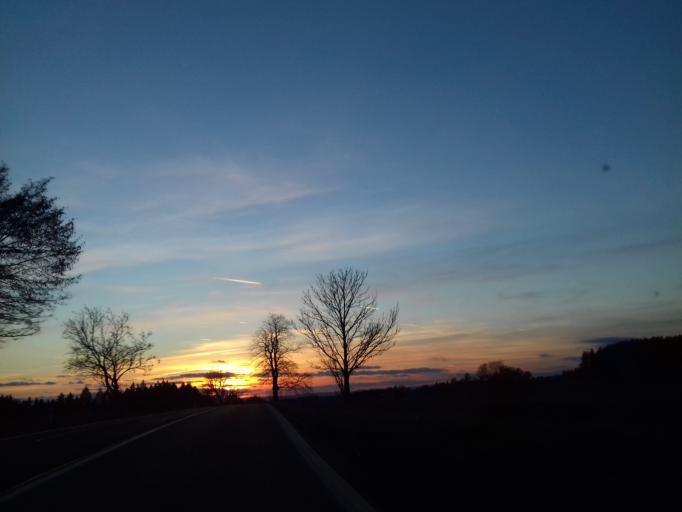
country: CZ
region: Vysocina
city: Chotebor
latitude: 49.6593
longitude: 15.7227
